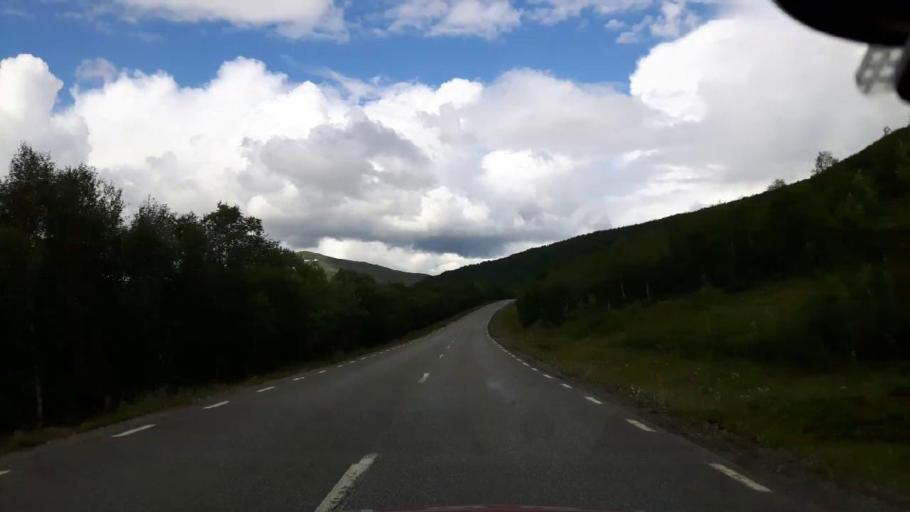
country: NO
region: Nordland
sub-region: Hattfjelldal
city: Hattfjelldal
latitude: 65.0633
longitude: 14.6974
